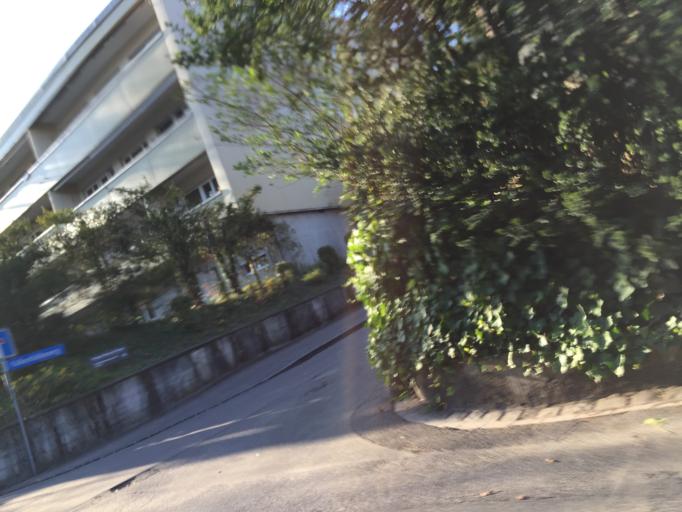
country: CH
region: Bern
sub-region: Bern-Mittelland District
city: Bern
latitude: 46.9503
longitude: 7.4337
